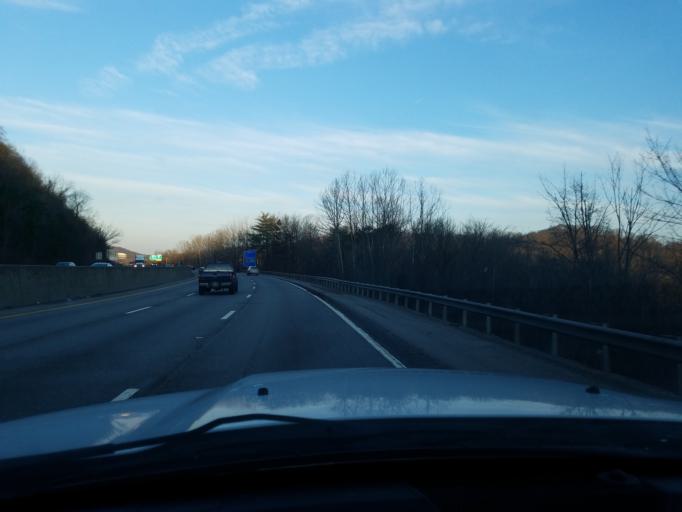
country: US
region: West Virginia
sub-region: Kanawha County
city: Cross Lanes
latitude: 38.4264
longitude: -81.8129
